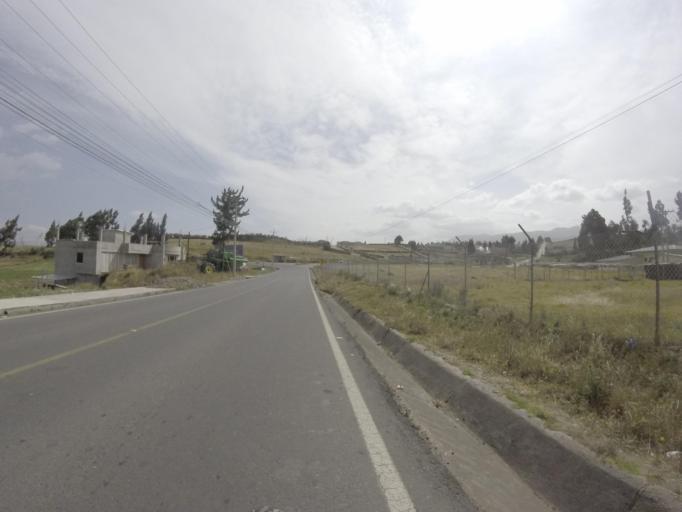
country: EC
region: Pichincha
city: Cayambe
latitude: 0.1329
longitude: -78.0821
